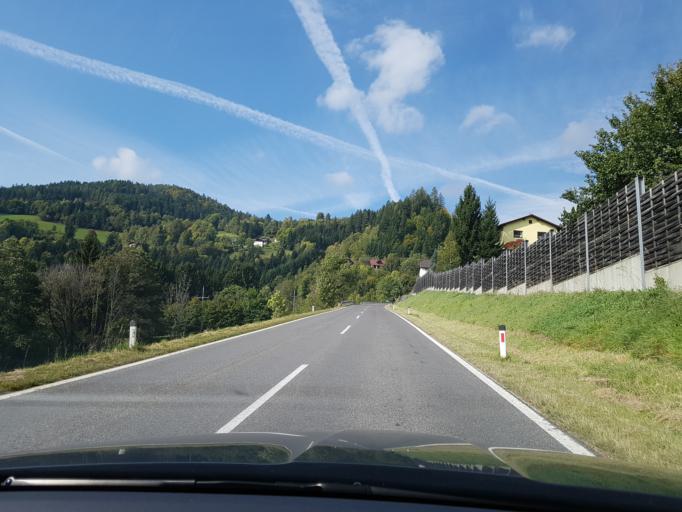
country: AT
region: Carinthia
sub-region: Politischer Bezirk Feldkirchen
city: Himmelberg
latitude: 46.7583
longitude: 14.0270
